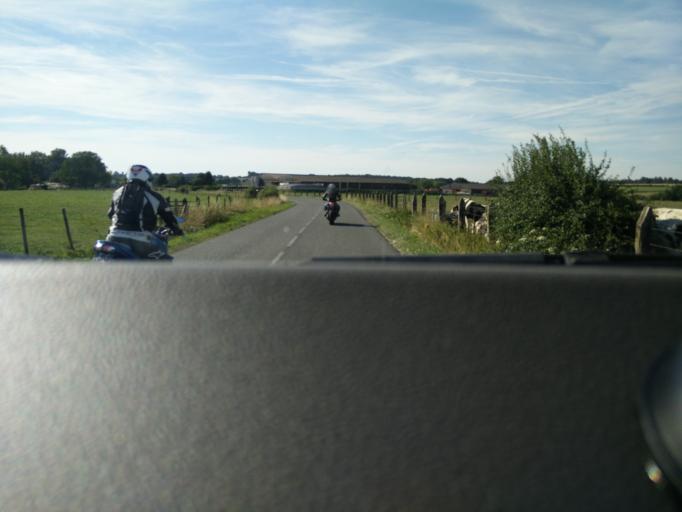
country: FR
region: Nord-Pas-de-Calais
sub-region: Departement du Nord
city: Sains-du-Nord
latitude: 50.1753
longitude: 4.0775
